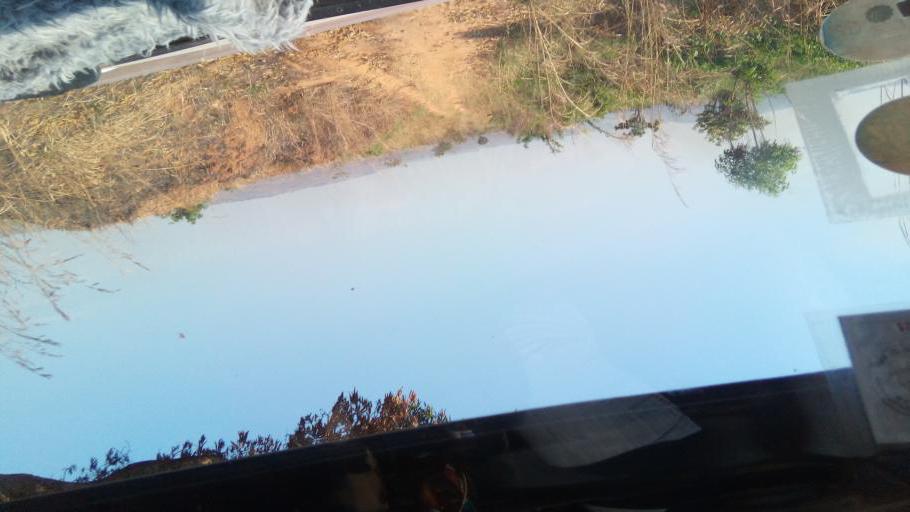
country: CD
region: Katanga
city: Kalemie
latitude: -5.9179
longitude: 29.1230
